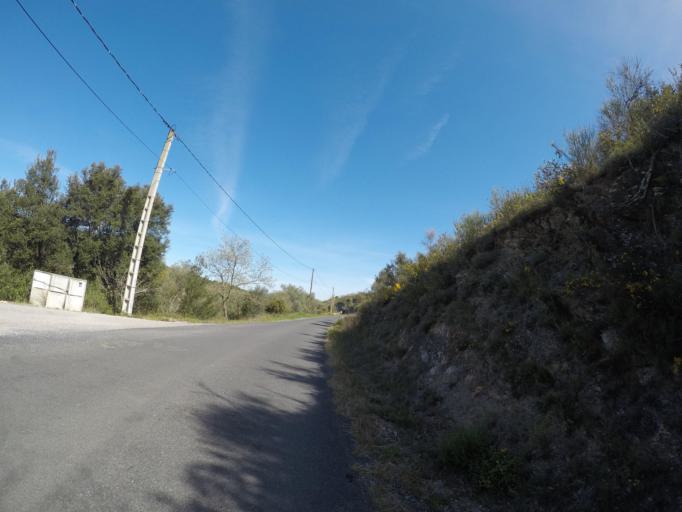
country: FR
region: Languedoc-Roussillon
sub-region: Departement des Pyrenees-Orientales
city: Thuir
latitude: 42.6361
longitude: 2.7002
